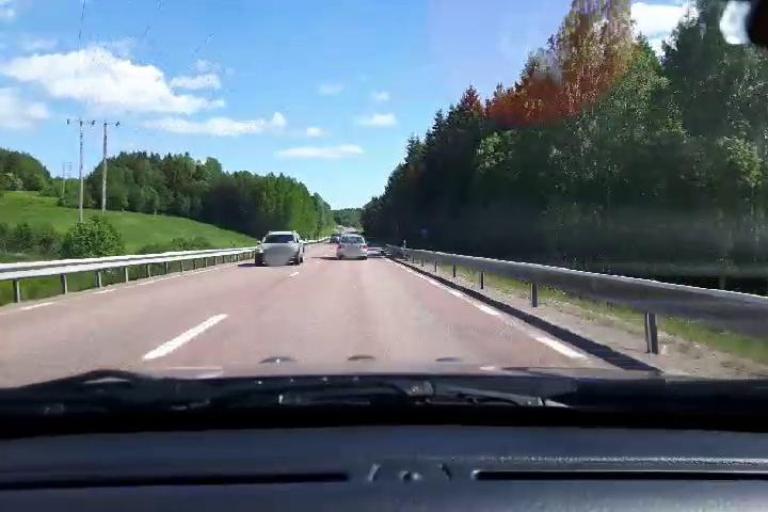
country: SE
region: Gaevleborg
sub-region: Hudiksvalls Kommun
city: Sorforsa
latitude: 61.7464
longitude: 16.8441
